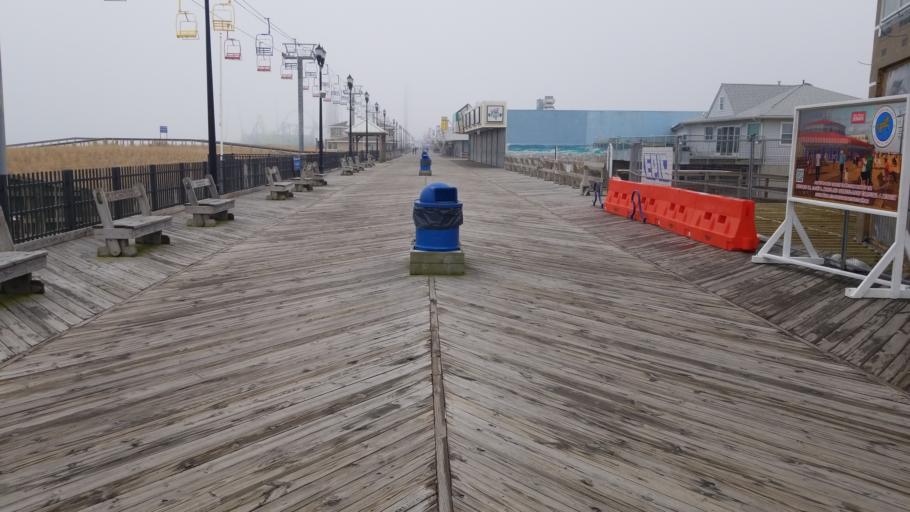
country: US
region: New Jersey
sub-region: Ocean County
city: Seaside Heights
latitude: 39.9467
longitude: -74.0696
